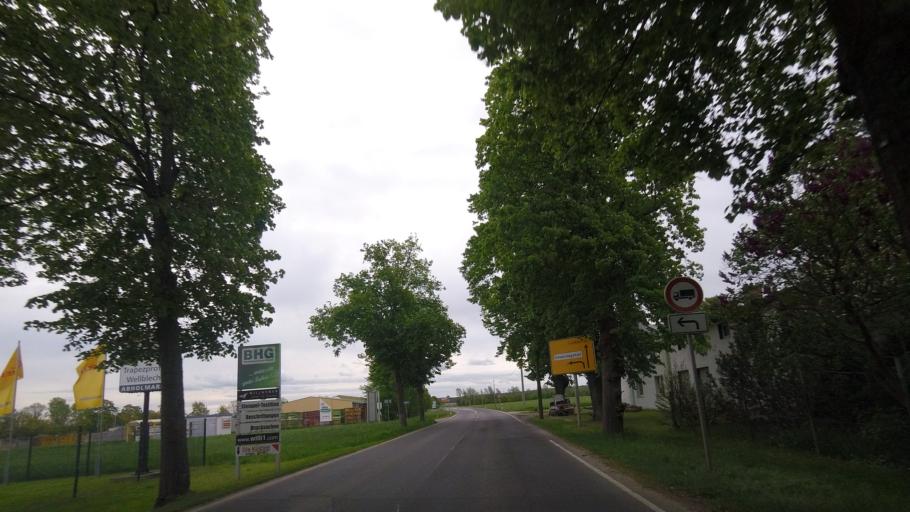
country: DE
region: Brandenburg
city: Dahme
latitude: 51.8643
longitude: 13.4403
